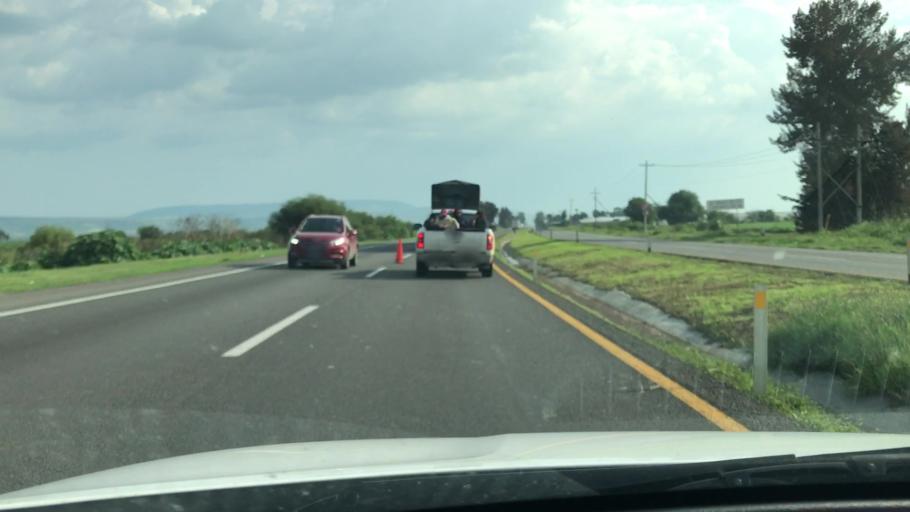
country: MX
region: Guanajuato
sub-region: Irapuato
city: San Ignacio de Rivera (Ojo de Agua)
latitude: 20.5171
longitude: -101.4656
